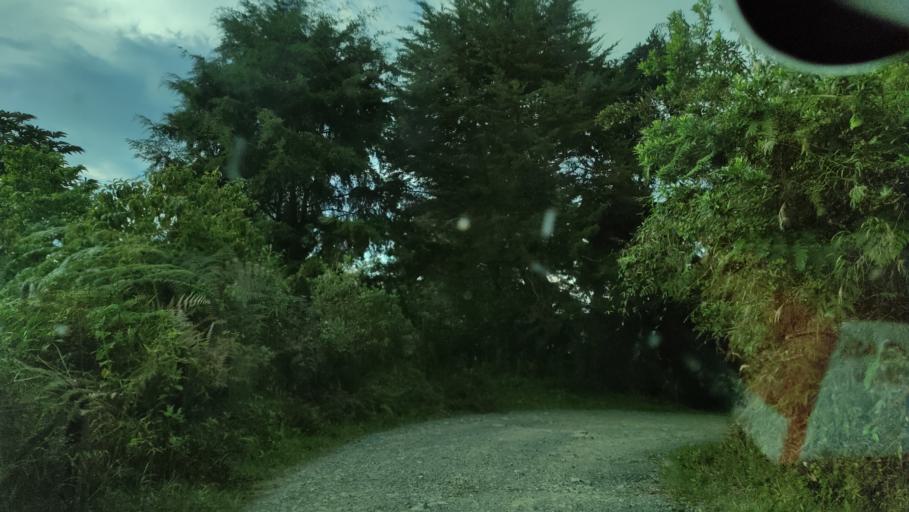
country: CO
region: Valle del Cauca
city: San Pedro
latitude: 3.8775
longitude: -76.1618
